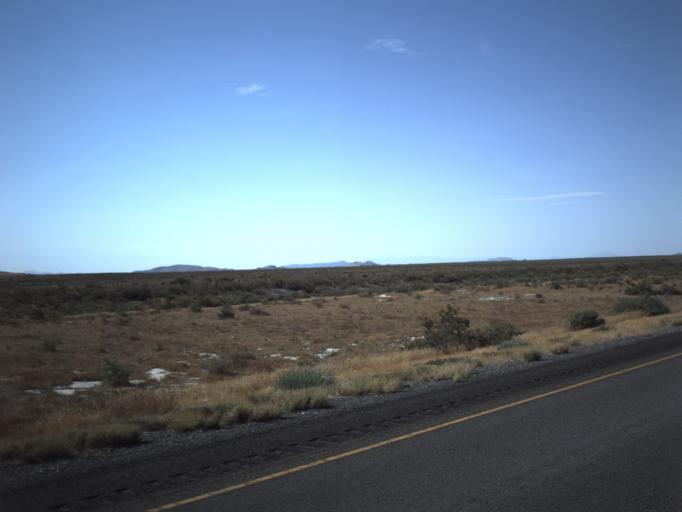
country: US
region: Utah
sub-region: Tooele County
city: Grantsville
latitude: 40.7438
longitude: -113.0724
